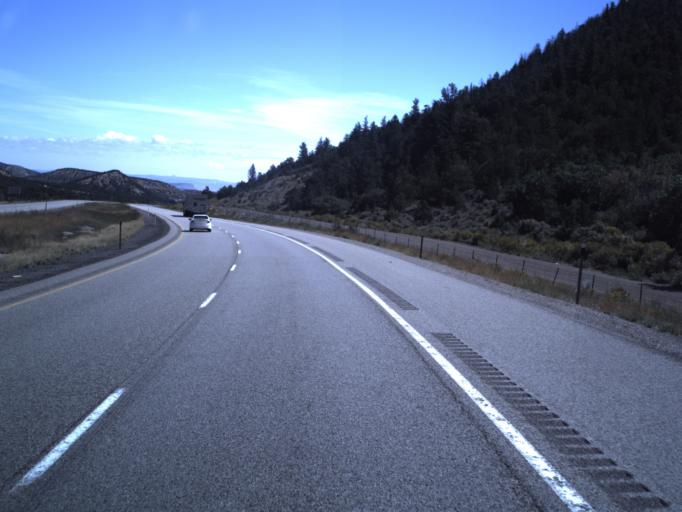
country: US
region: Utah
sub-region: Wayne County
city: Loa
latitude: 38.7561
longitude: -111.4428
